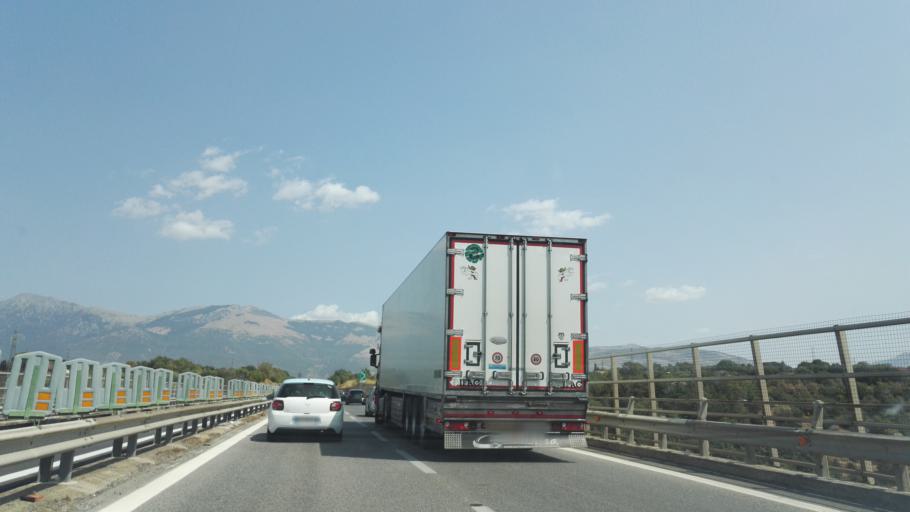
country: IT
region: Calabria
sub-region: Provincia di Cosenza
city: Castrovillari
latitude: 39.7816
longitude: 16.2243
